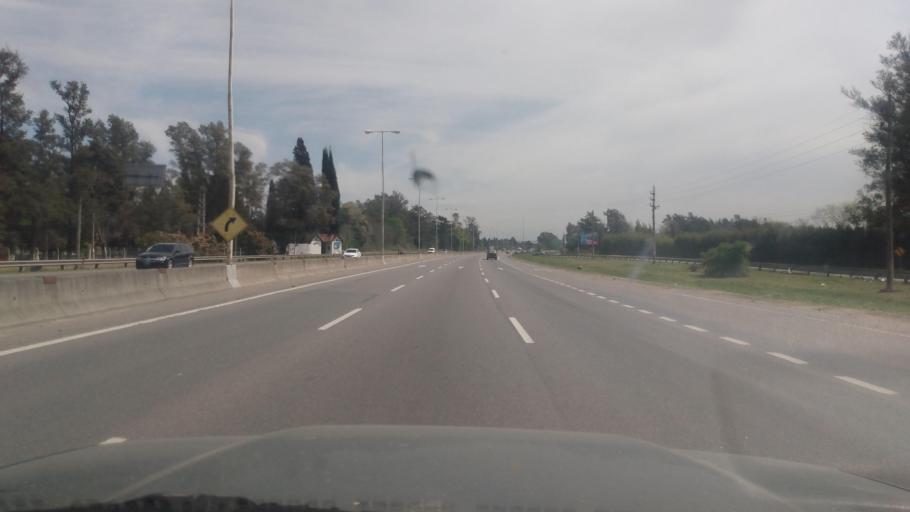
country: AR
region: Buenos Aires
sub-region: Partido de Pilar
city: Pilar
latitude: -34.4383
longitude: -58.9788
